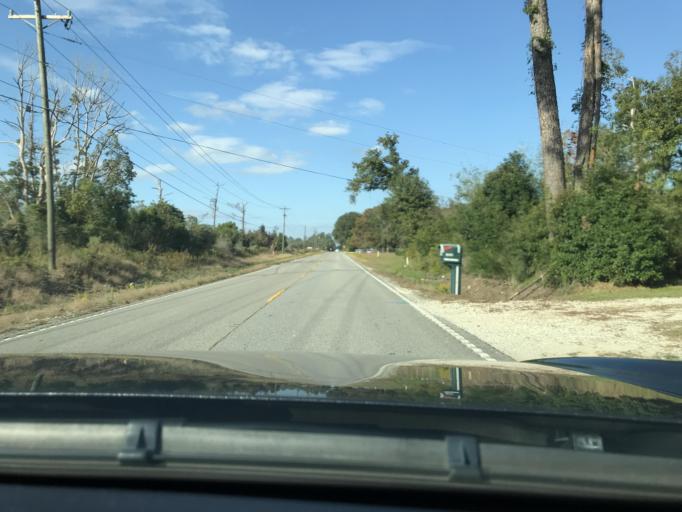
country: US
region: Louisiana
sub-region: Calcasieu Parish
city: Moss Bluff
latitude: 30.3190
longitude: -93.2582
